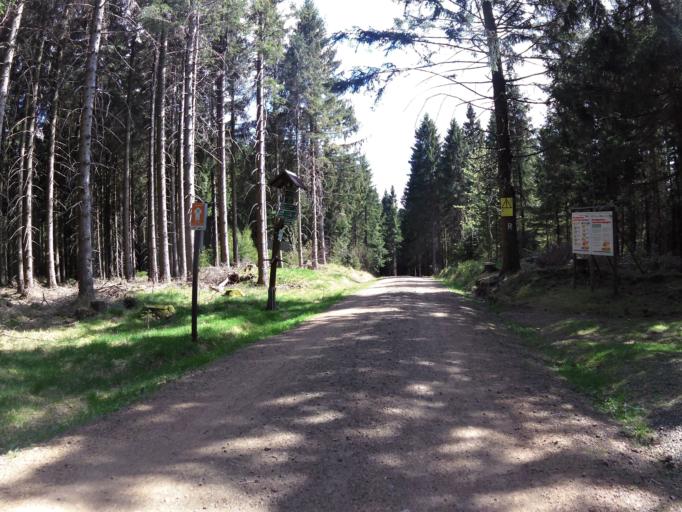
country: DE
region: Thuringia
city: Tambach-Dietharz
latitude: 50.7731
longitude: 10.5664
